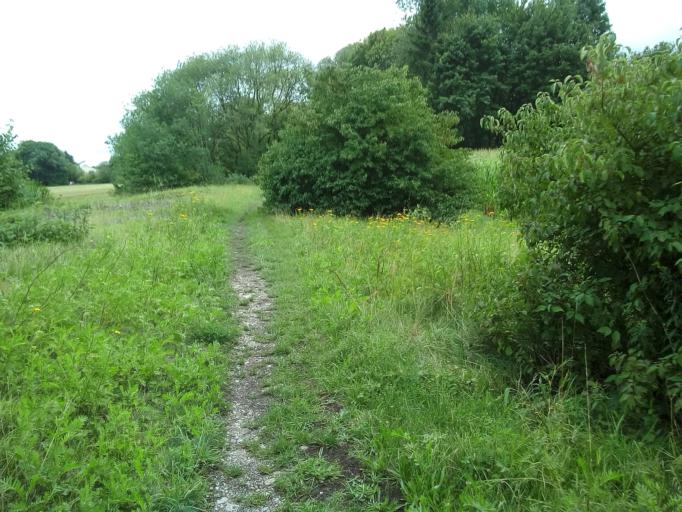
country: DE
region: Bavaria
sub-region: Upper Bavaria
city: Aschheim
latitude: 48.1645
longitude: 11.6786
